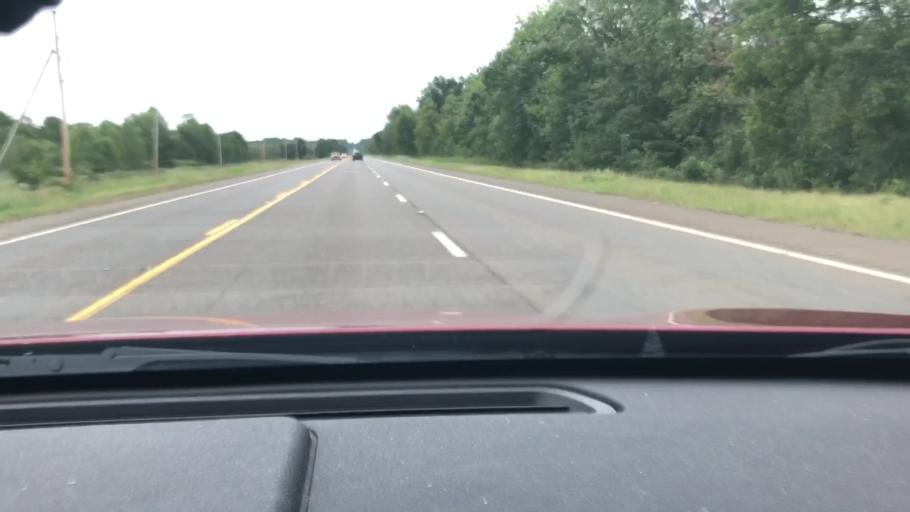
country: US
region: Arkansas
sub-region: Lafayette County
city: Lewisville
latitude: 33.3571
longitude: -93.6458
